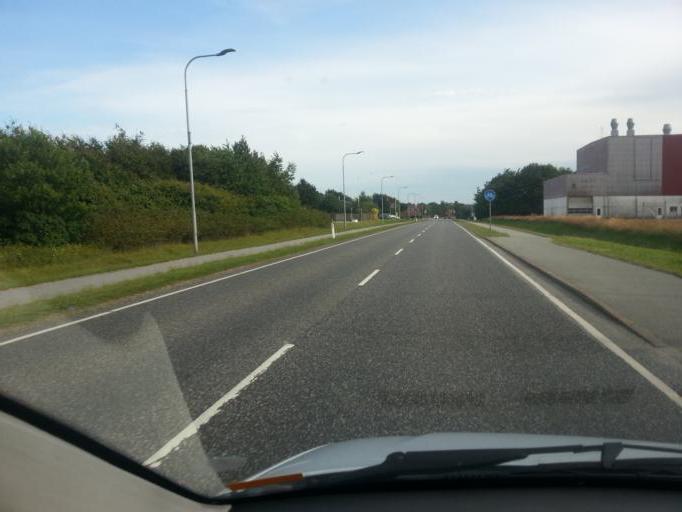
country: DK
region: South Denmark
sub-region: Vejen Kommune
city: Holsted
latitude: 55.4927
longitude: 8.9149
